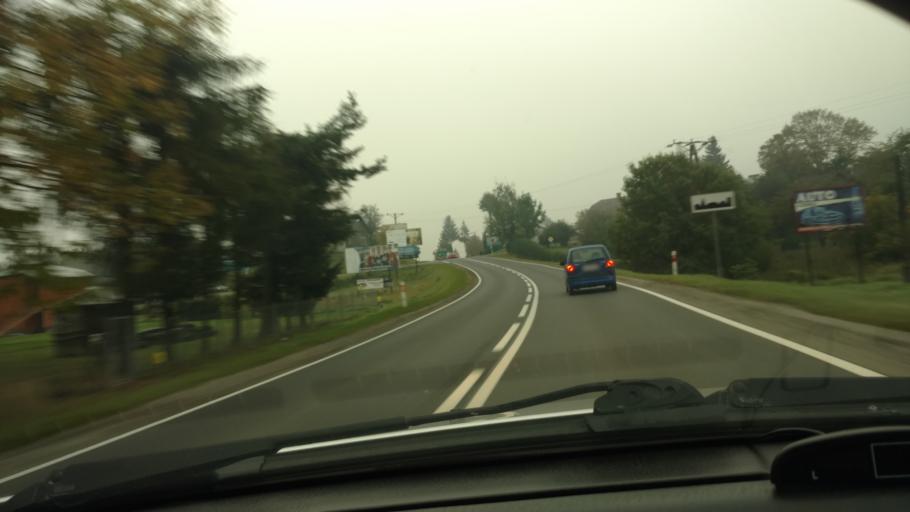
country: PL
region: Subcarpathian Voivodeship
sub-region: Powiat strzyzowski
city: Frysztak
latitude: 49.8325
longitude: 21.6146
